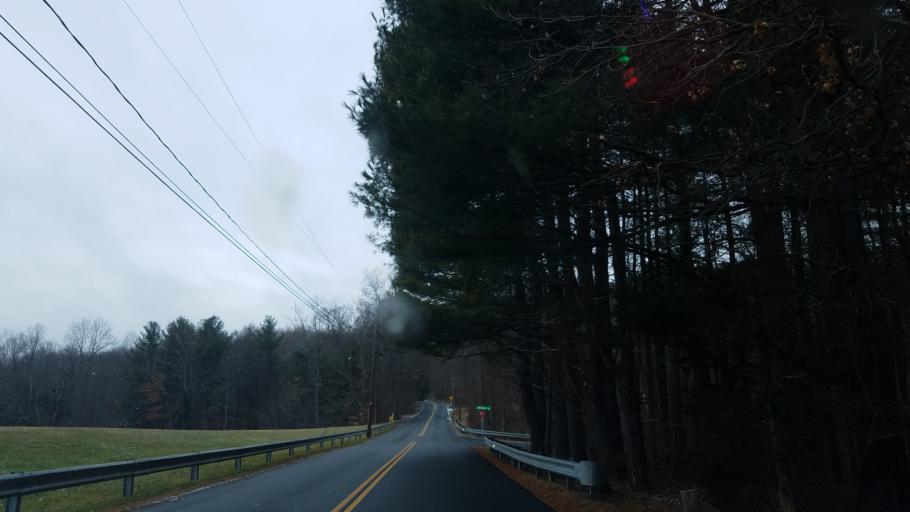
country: US
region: Connecticut
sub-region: Hartford County
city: Kensington
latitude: 41.6140
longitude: -72.8095
